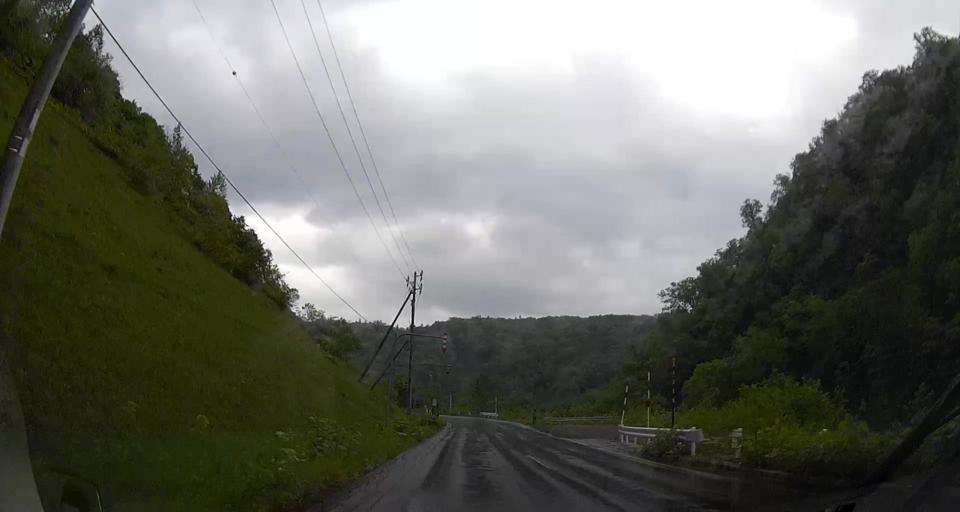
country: JP
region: Hokkaido
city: Niseko Town
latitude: 42.9058
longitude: 140.9178
